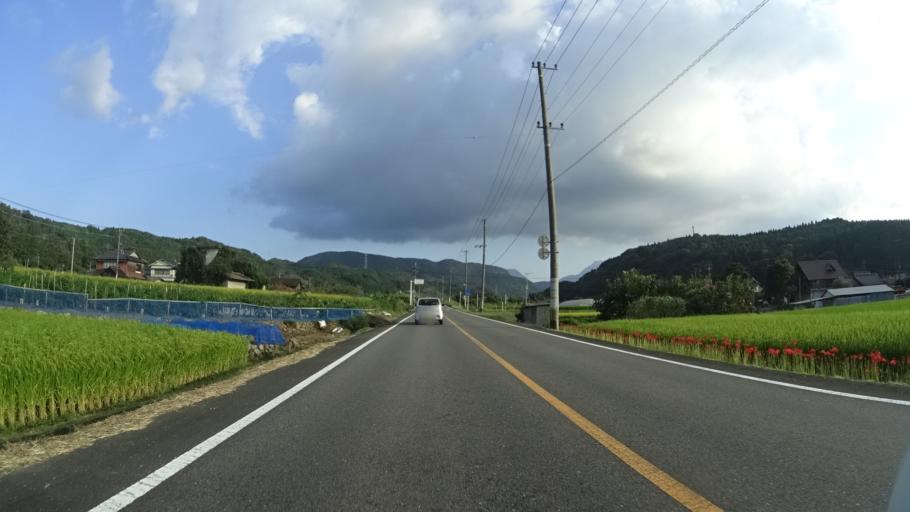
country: JP
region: Oita
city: Hiji
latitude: 33.3904
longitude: 131.3942
